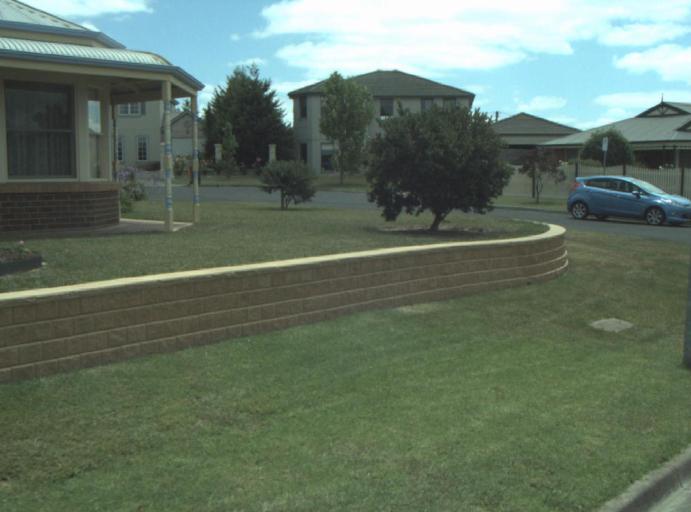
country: AU
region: Victoria
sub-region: Greater Geelong
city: Wandana Heights
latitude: -38.1888
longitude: 144.3224
